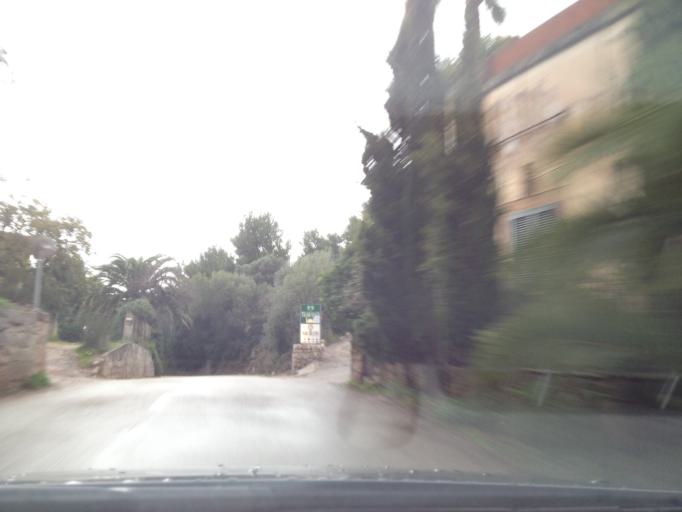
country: ES
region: Balearic Islands
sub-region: Illes Balears
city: Deia
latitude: 39.7733
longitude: 2.6766
